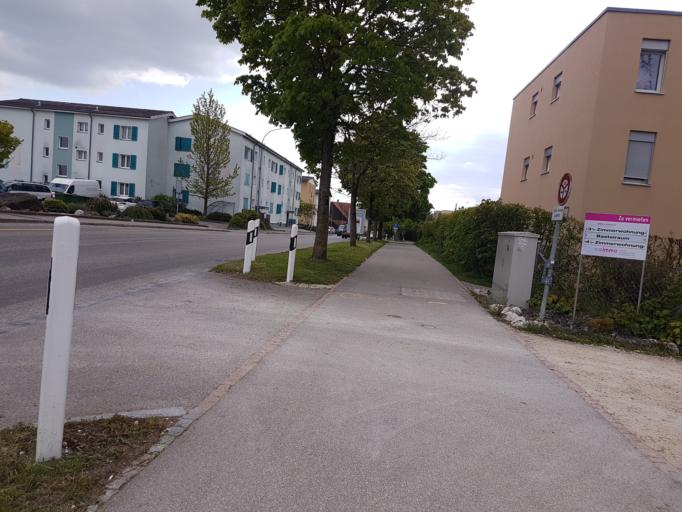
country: CH
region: Bern
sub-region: Biel/Bienne District
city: Orpund
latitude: 47.1410
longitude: 7.3151
